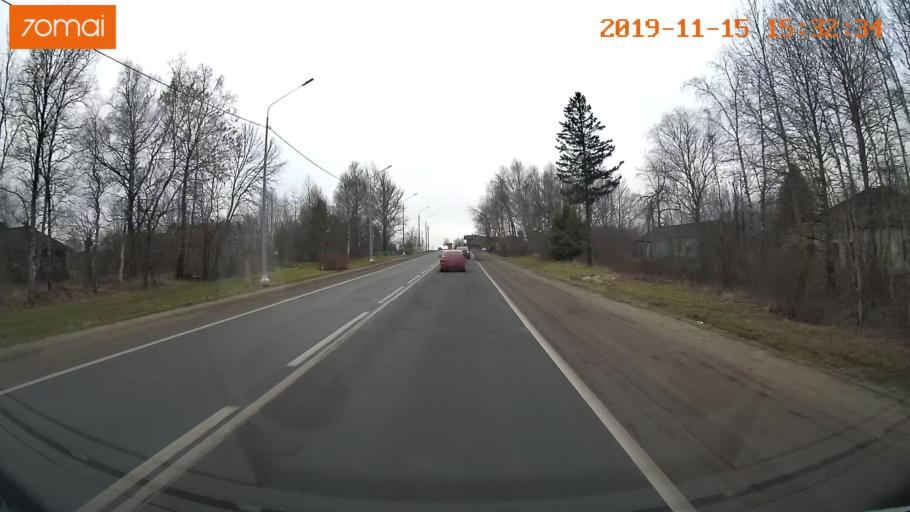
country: RU
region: Jaroslavl
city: Danilov
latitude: 58.0890
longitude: 40.0987
